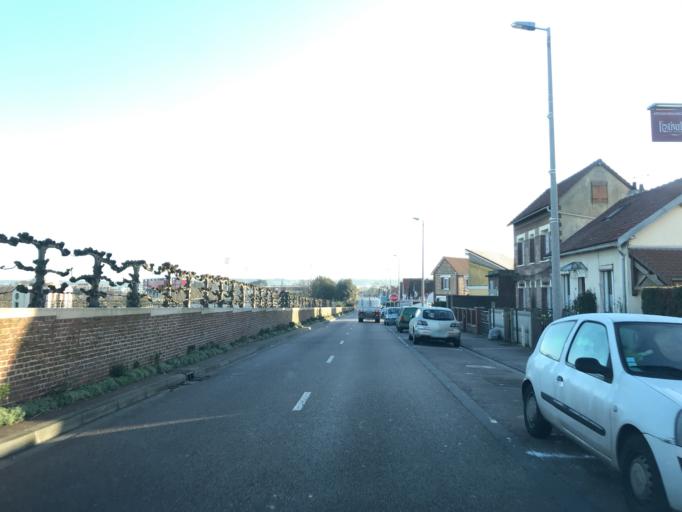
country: FR
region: Haute-Normandie
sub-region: Departement de la Seine-Maritime
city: Le Petit-Quevilly
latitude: 49.4079
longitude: 1.0643
